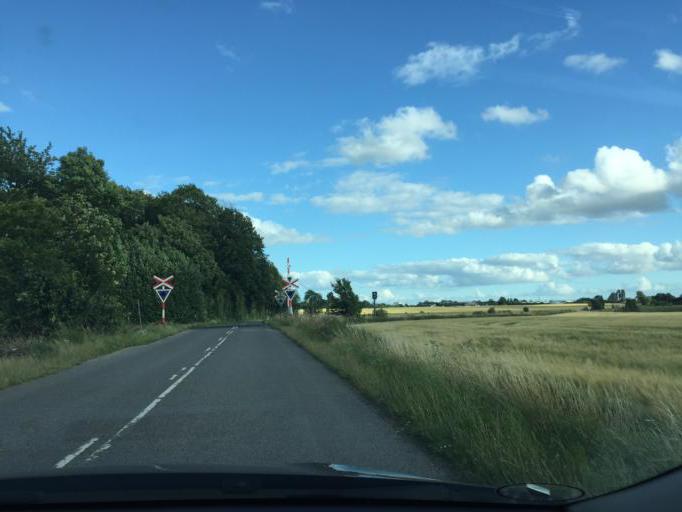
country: DK
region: South Denmark
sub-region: Faaborg-Midtfyn Kommune
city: Ringe
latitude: 55.2617
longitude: 10.4781
